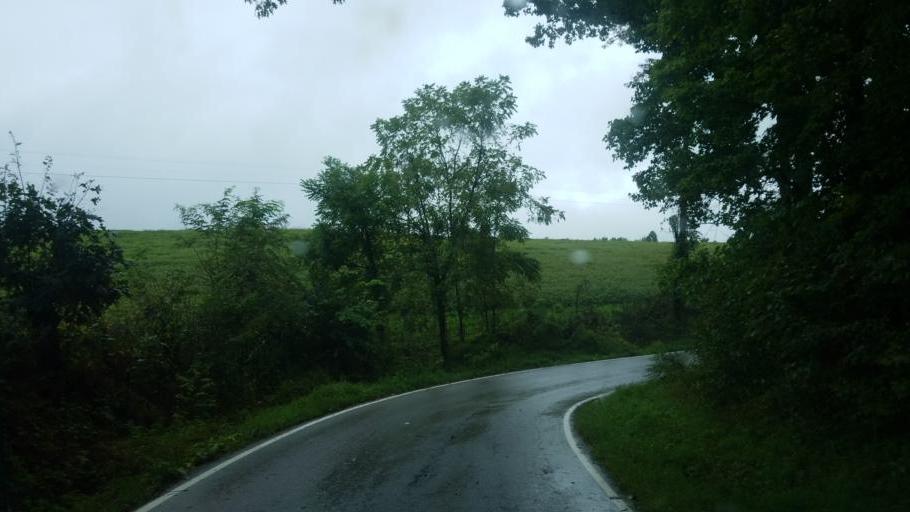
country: US
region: Kentucky
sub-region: Fleming County
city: Flemingsburg
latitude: 38.4728
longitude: -83.5129
